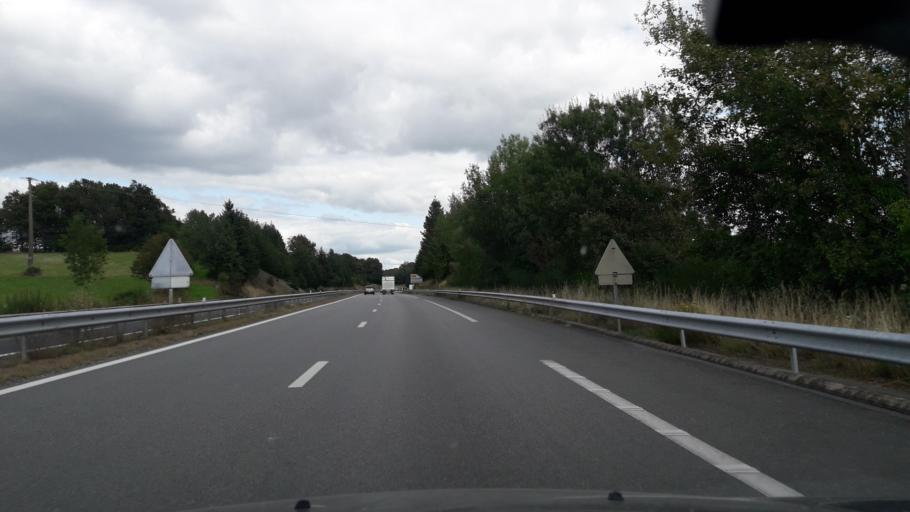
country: FR
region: Limousin
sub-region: Departement de la Creuse
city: Ajain
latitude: 46.2022
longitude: 1.9805
